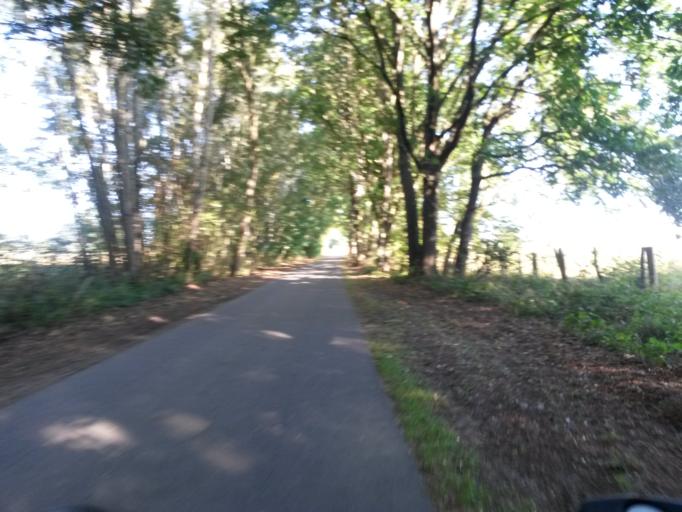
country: DE
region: Brandenburg
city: Templin
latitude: 53.1344
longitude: 13.4509
